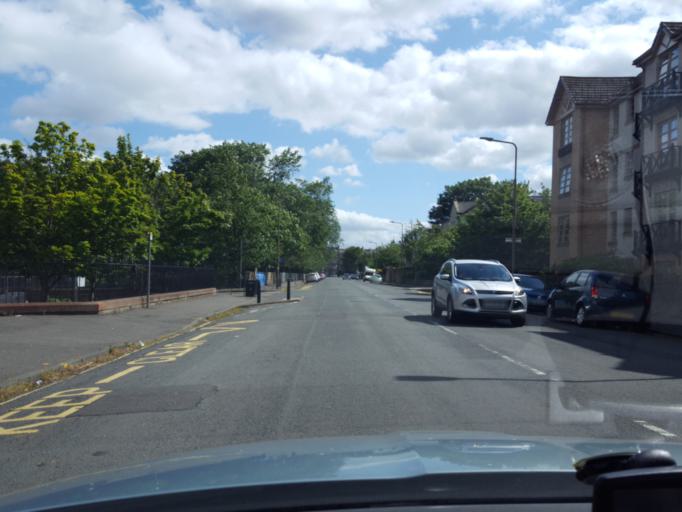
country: GB
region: Scotland
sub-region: Edinburgh
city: Edinburgh
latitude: 55.9764
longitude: -3.1969
